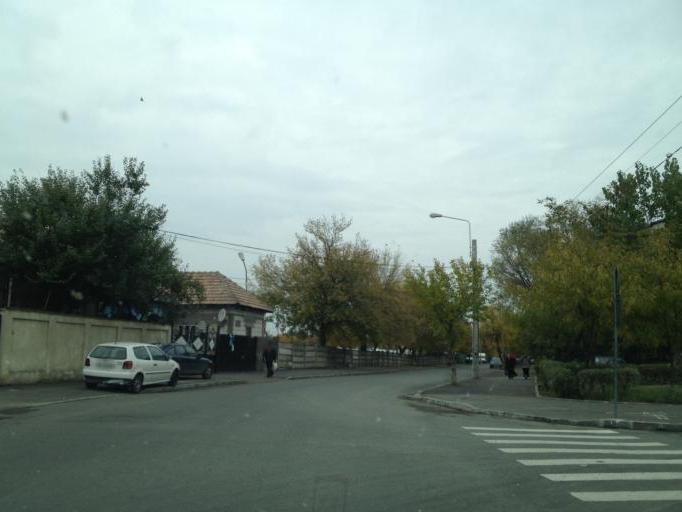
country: RO
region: Dolj
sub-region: Municipiul Craiova
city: Popoveni
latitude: 44.2977
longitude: 23.7902
